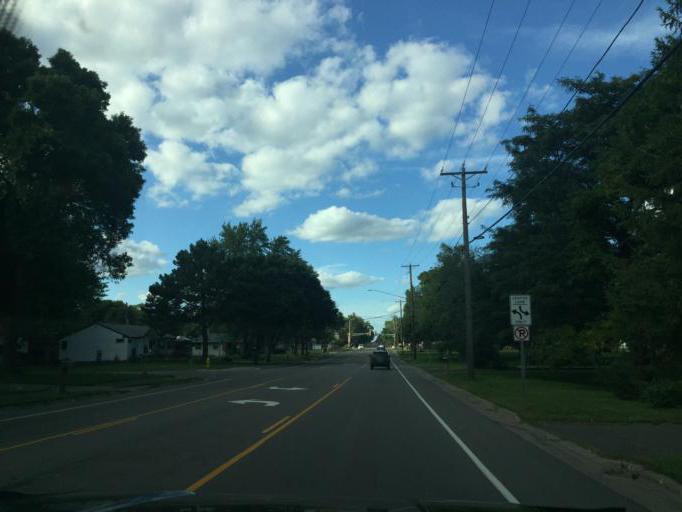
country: US
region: Minnesota
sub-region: Ramsey County
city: Roseville
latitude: 44.9970
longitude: -93.1463
